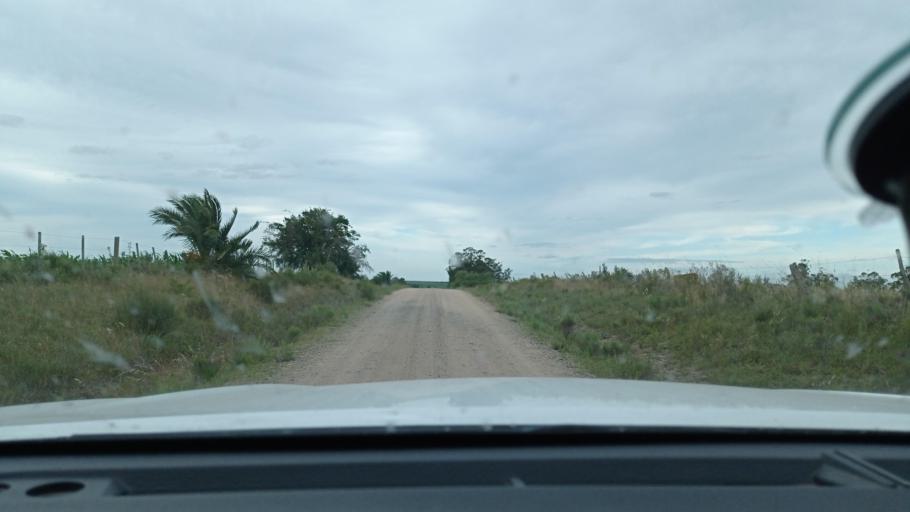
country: UY
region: Florida
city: Casupa
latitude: -34.1330
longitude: -55.7801
